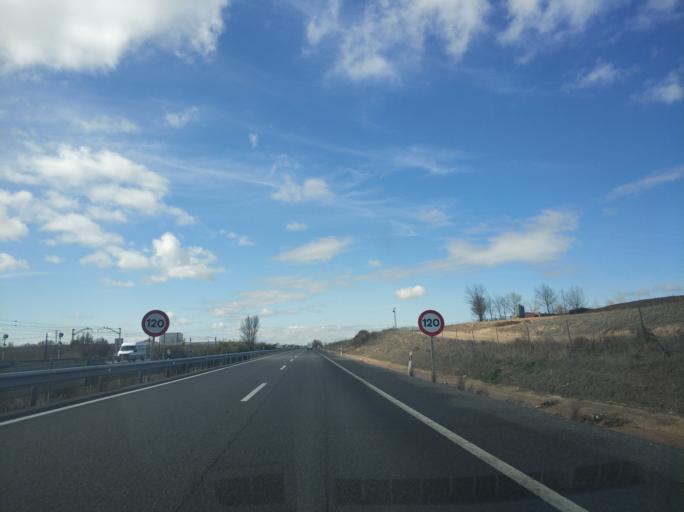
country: ES
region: Castille and Leon
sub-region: Provincia de Burgos
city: Estepar
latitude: 42.2849
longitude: -3.8662
